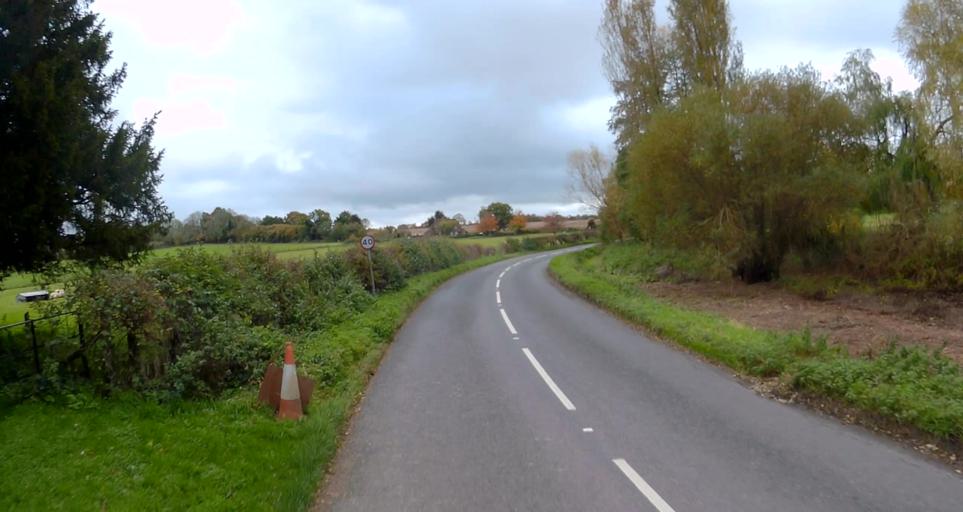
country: GB
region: England
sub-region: Hampshire
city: Four Marks
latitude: 51.1564
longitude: -1.1551
